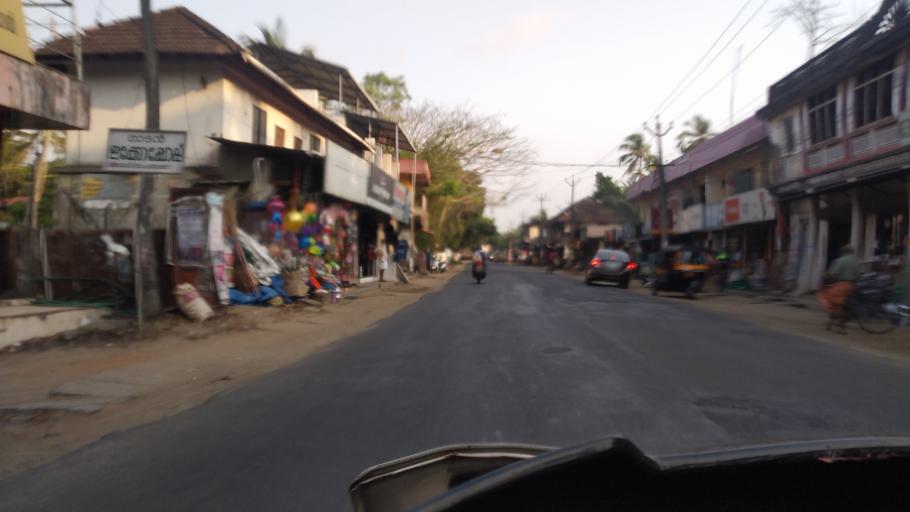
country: IN
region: Kerala
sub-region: Thrissur District
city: Thanniyam
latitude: 10.4036
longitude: 76.1120
